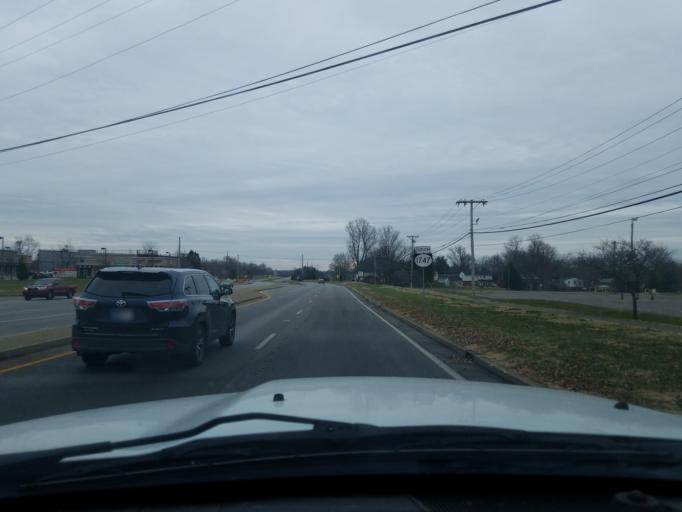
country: US
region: Kentucky
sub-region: Jefferson County
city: Worthington
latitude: 38.2872
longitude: -85.5721
